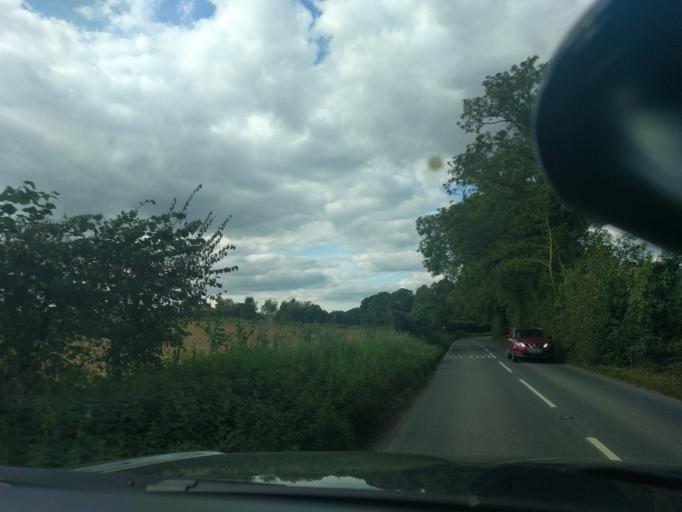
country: GB
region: England
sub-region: Wiltshire
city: Bradford-on-Avon
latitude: 51.3694
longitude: -2.2358
